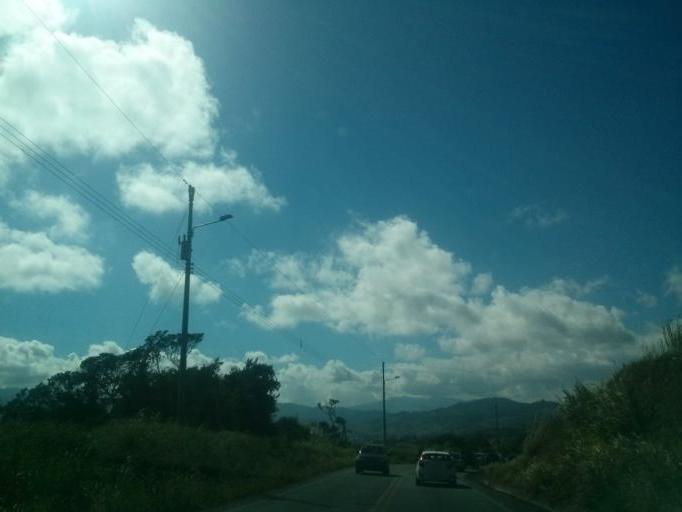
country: CR
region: Cartago
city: Cot
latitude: 9.8840
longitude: -83.8911
